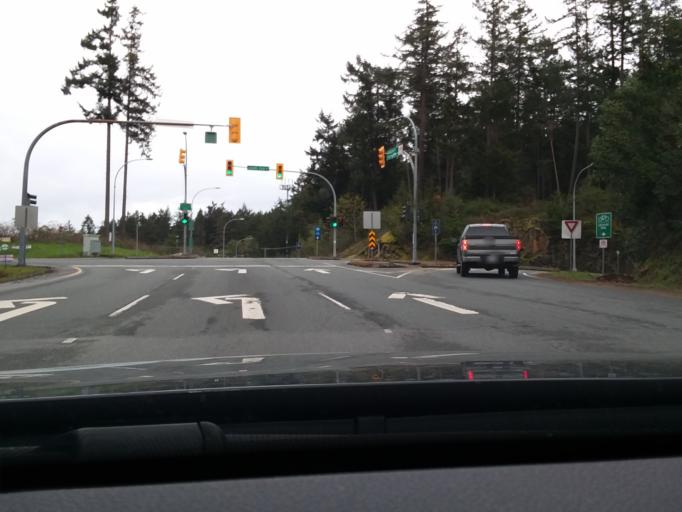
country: CA
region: British Columbia
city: North Saanich
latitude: 48.6830
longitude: -123.4124
